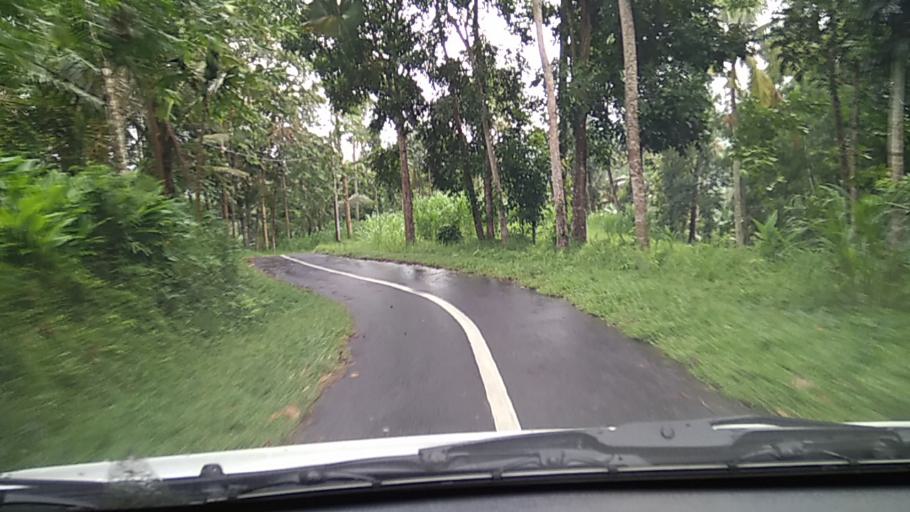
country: ID
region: Bali
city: Tiyingtali Kelod
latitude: -8.4007
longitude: 115.6296
